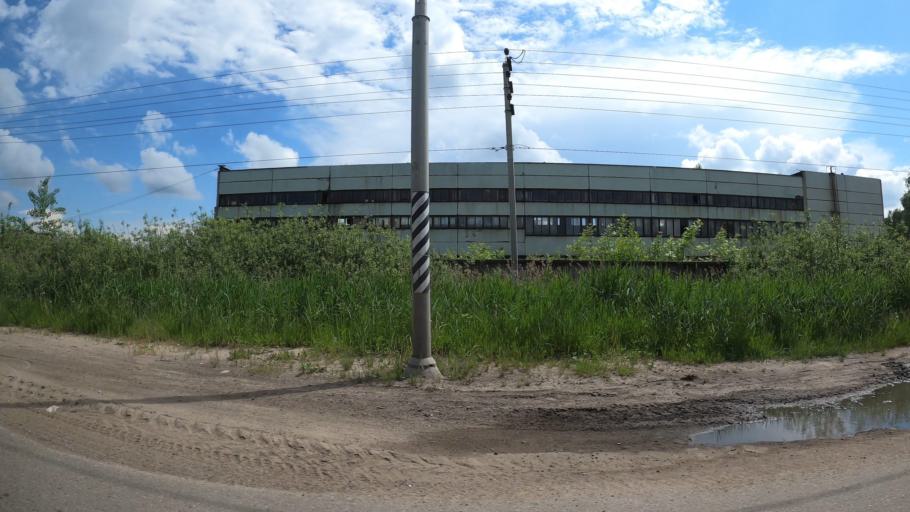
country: RU
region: Moskovskaya
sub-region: Shchelkovskiy Rayon
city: Grebnevo
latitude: 55.9665
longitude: 38.0828
